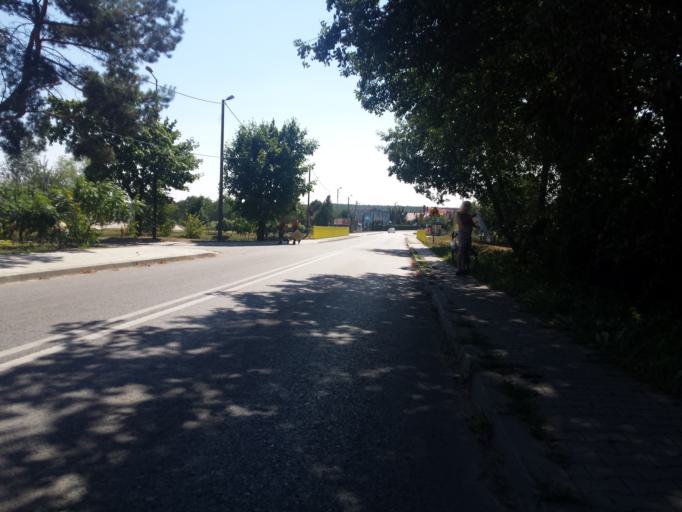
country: PL
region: Swietokrzyskie
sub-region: Powiat kielecki
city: Daleszyce
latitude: 50.7744
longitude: 20.7502
